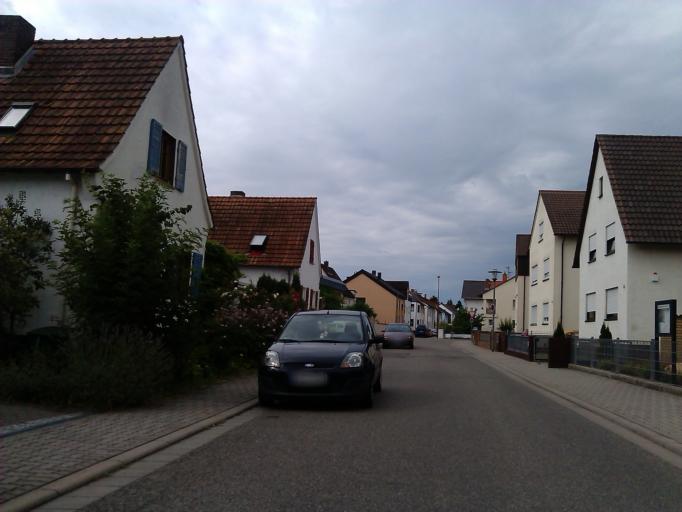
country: DE
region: Rheinland-Pfalz
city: Schifferstadt
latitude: 49.3777
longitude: 8.3853
